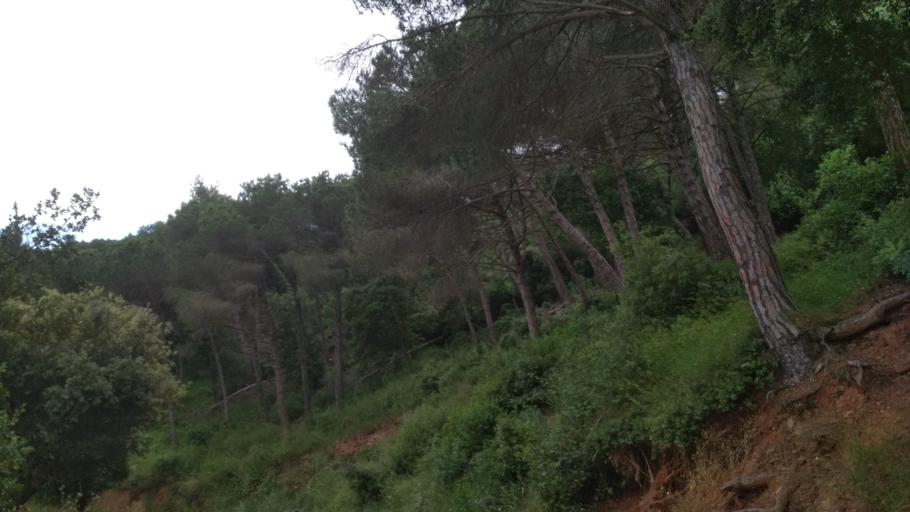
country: ES
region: Catalonia
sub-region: Provincia de Barcelona
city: Nou Barris
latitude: 41.4531
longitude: 2.1661
